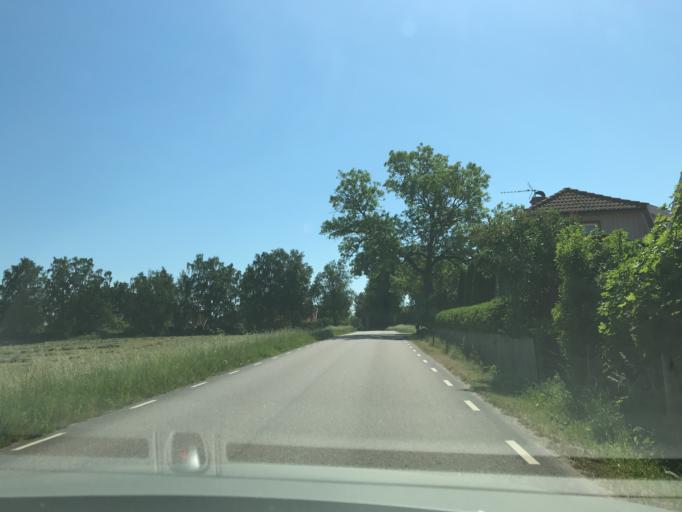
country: SE
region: Vaestra Goetaland
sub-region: Gotene Kommun
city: Kallby
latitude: 58.5362
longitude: 13.3224
